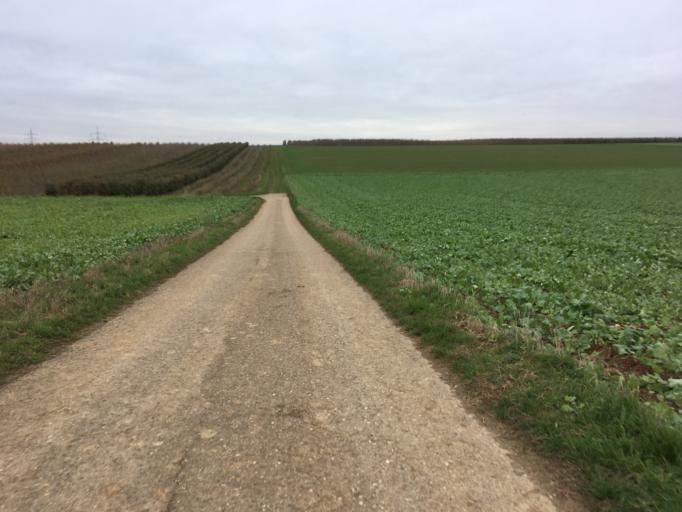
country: DE
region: Baden-Wuerttemberg
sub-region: Regierungsbezirk Stuttgart
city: Lauffen am Neckar
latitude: 49.0774
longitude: 9.1257
